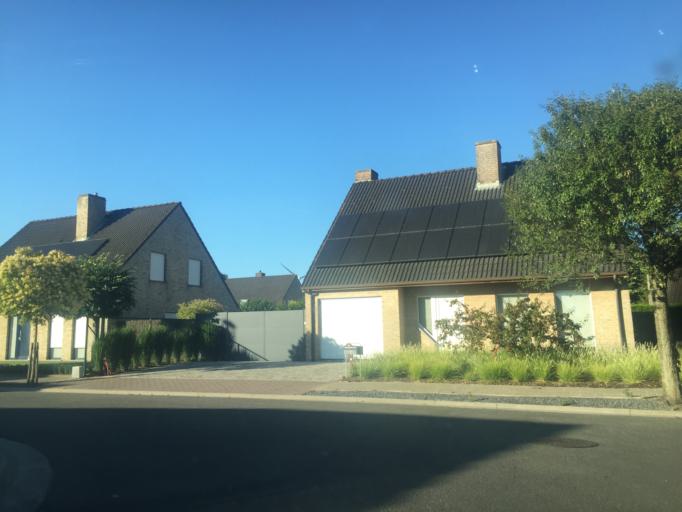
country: BE
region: Flanders
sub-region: Provincie West-Vlaanderen
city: Izegem
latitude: 50.9213
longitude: 3.1914
